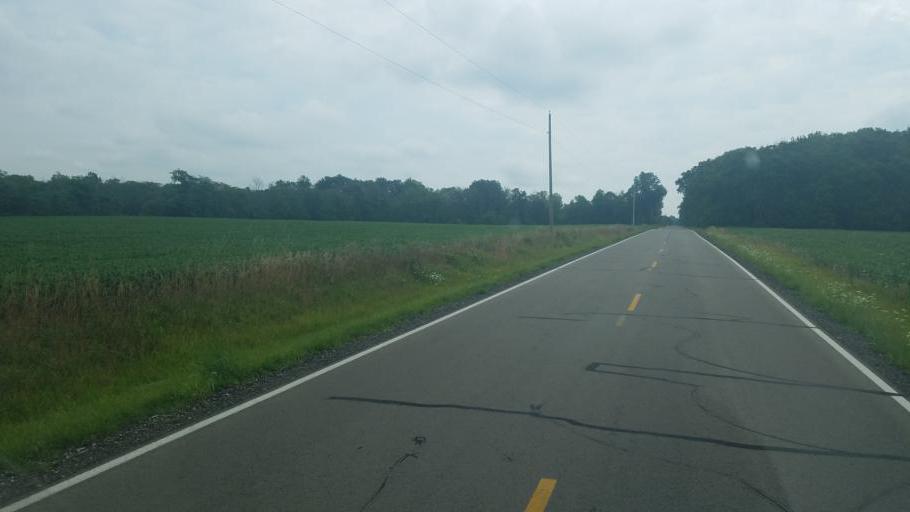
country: US
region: Ohio
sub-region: Crawford County
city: Galion
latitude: 40.7197
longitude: -82.8464
